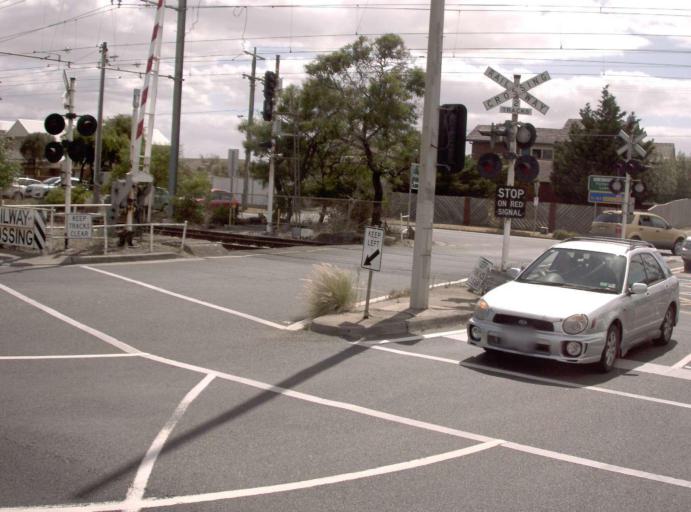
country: AU
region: Victoria
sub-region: Kingston
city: Bonbeach
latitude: -38.0748
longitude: 145.1222
